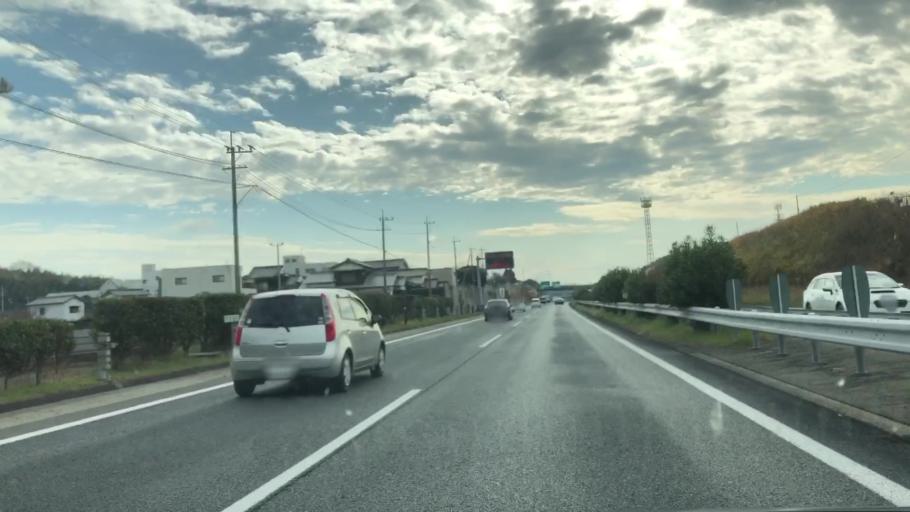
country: JP
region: Fukuoka
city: Kurume
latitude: 33.2609
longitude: 130.5382
